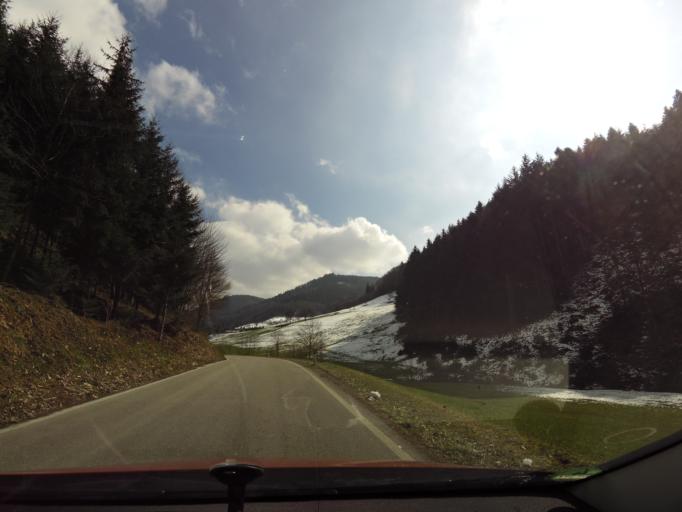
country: DE
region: Baden-Wuerttemberg
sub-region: Freiburg Region
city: Ottenhofen im Schwarzwald
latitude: 48.5516
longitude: 8.1584
